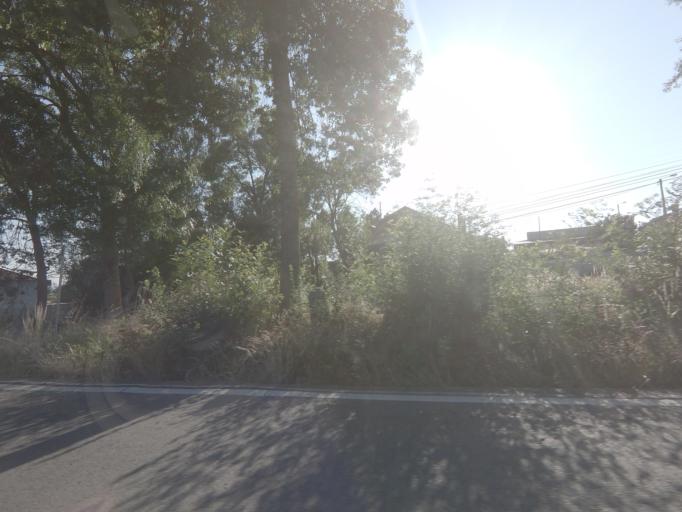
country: PT
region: Vila Real
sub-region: Chaves
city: Chaves
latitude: 41.7951
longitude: -7.4232
